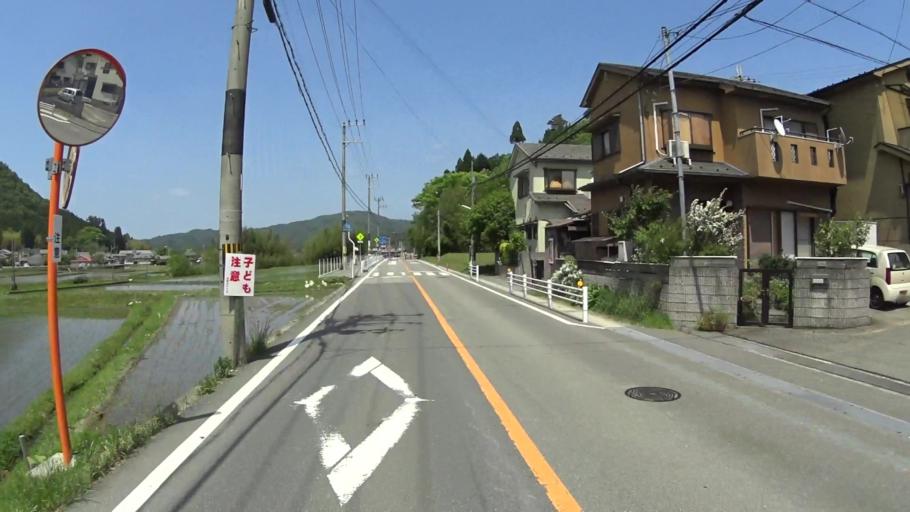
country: JP
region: Kyoto
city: Kameoka
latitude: 35.0099
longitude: 135.4849
